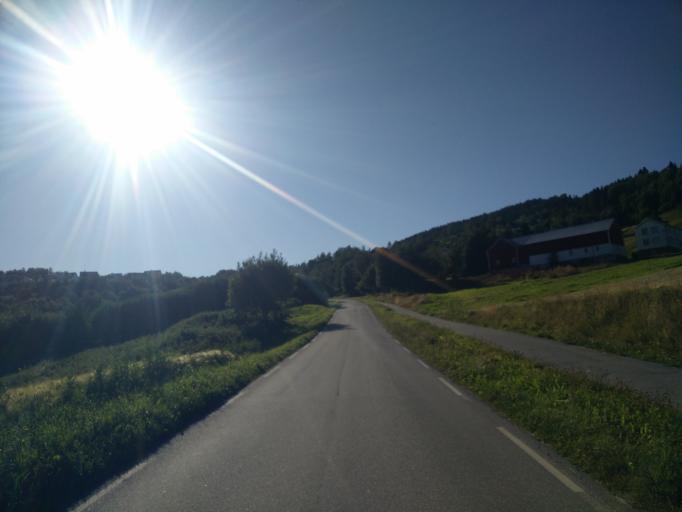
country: NO
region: Sor-Trondelag
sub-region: Skaun
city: Borsa
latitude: 63.3260
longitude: 10.0569
